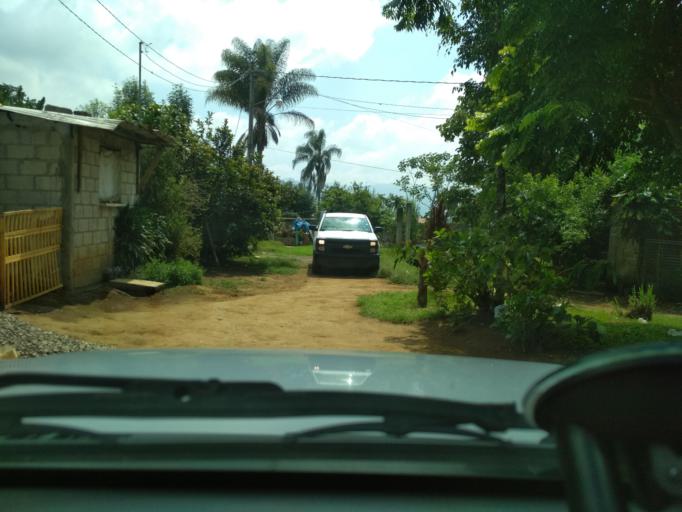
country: MX
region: Veracruz
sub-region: Fortin
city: Santa Lucia Potrerillo
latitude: 18.9693
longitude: -97.0265
